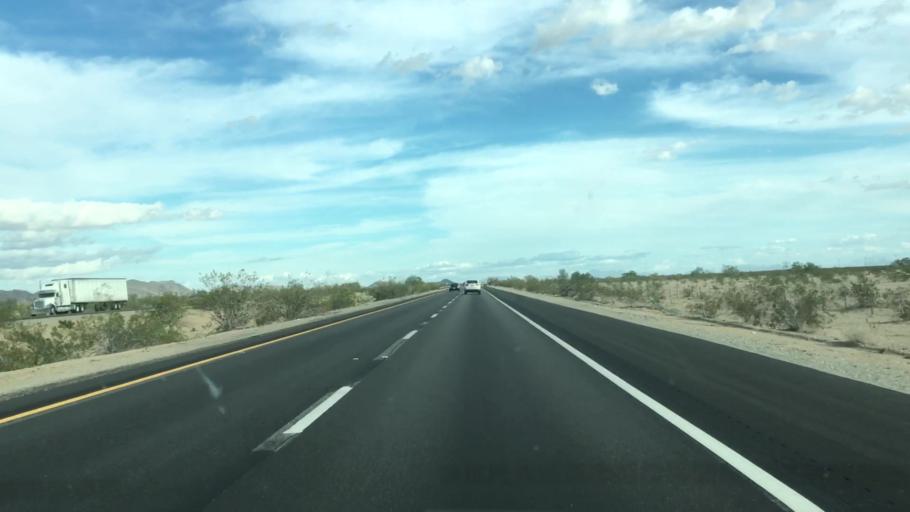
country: US
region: California
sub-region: Riverside County
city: Mesa Verde
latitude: 33.6093
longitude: -114.8501
